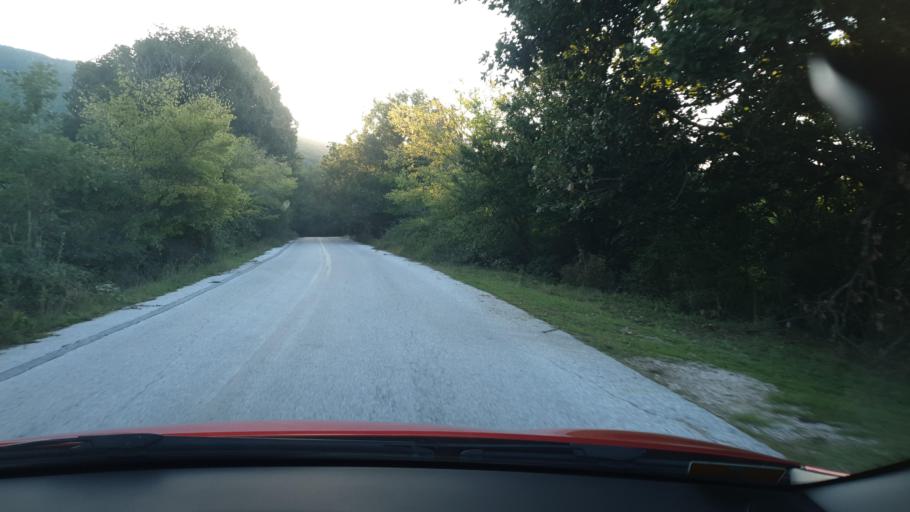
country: GR
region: Central Macedonia
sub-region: Nomos Chalkidikis
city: Galatista
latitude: 40.5037
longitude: 23.2306
